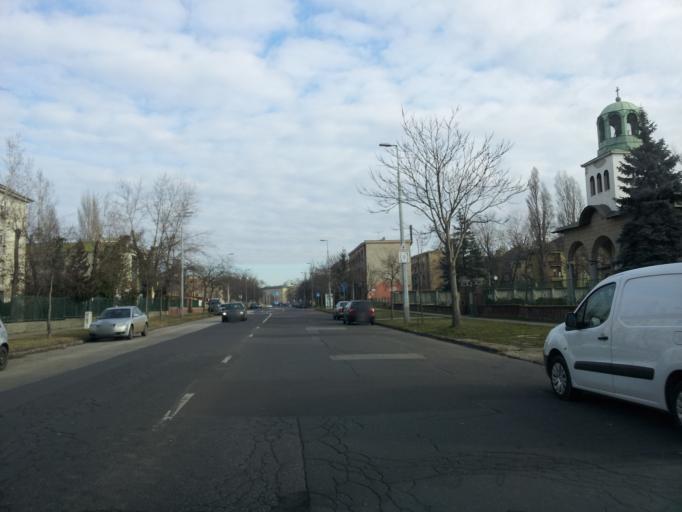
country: HU
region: Budapest
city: Budapest IX. keruelet
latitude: 47.4748
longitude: 19.0843
